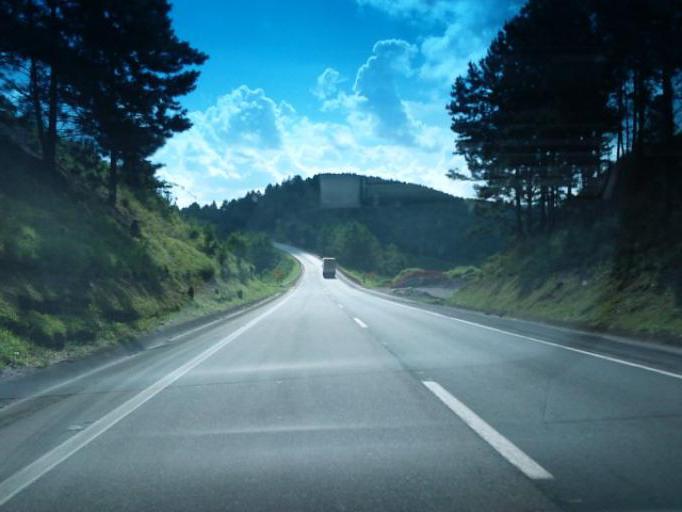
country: BR
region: Parana
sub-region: Campina Grande Do Sul
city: Campina Grande do Sul
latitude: -25.1055
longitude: -48.8444
